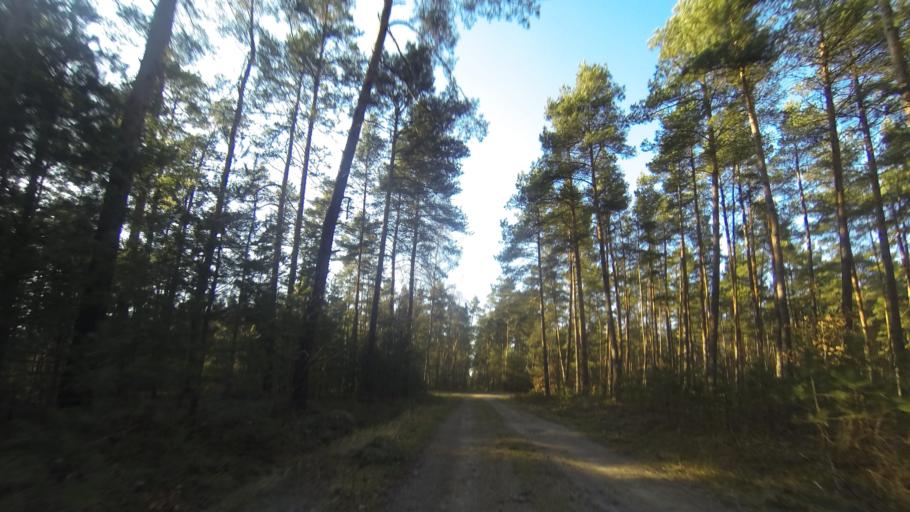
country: DE
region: Saxony
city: Tauscha
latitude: 51.2190
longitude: 13.7946
